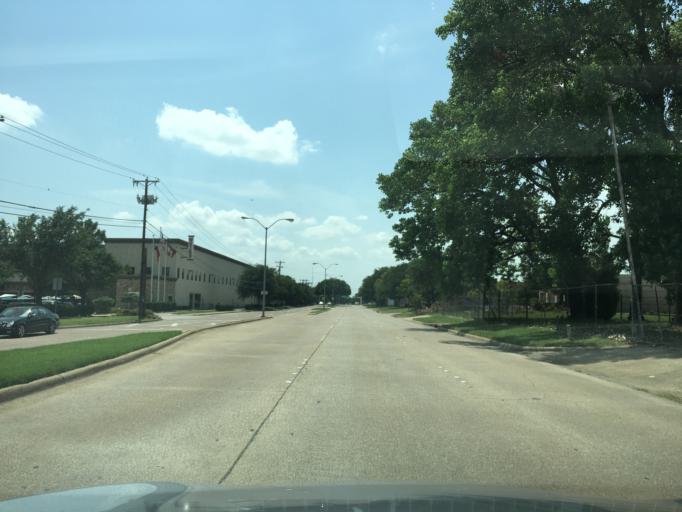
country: US
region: Texas
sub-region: Dallas County
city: Addison
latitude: 32.9397
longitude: -96.8262
